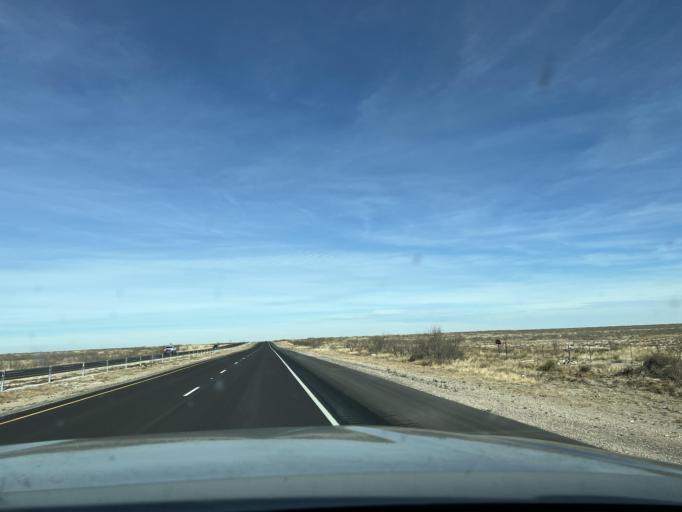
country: US
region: Texas
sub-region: Ector County
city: Gardendale
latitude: 32.0304
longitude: -102.4324
